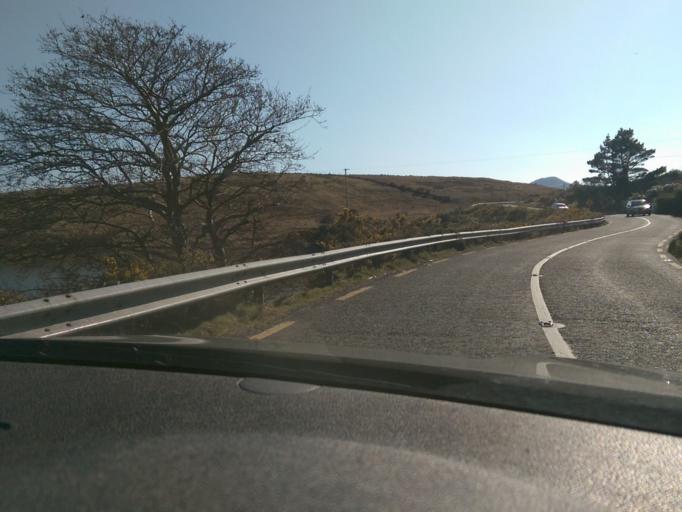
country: IE
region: Connaught
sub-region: County Galway
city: Clifden
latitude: 53.4626
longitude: -9.7587
